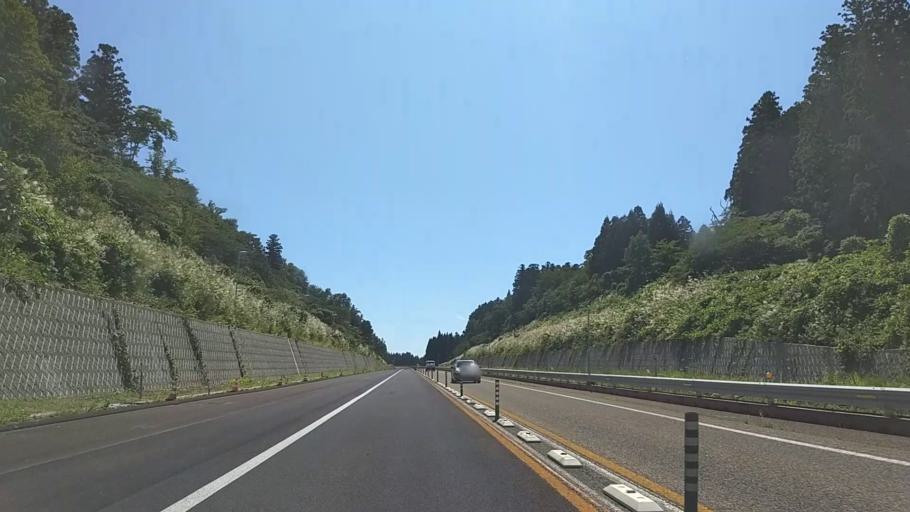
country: JP
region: Niigata
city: Arai
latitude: 37.0004
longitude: 138.2076
